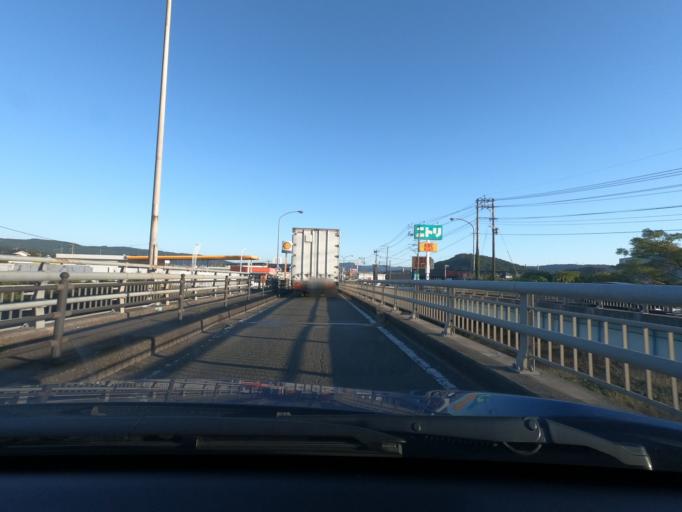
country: JP
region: Kagoshima
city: Satsumasendai
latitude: 31.8369
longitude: 130.2866
